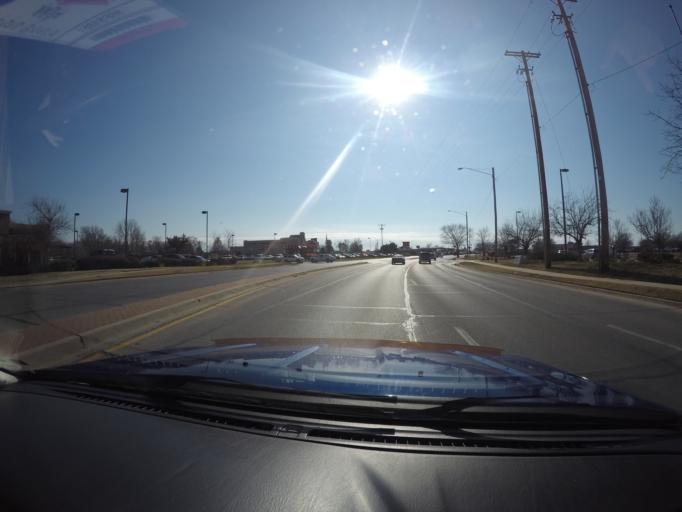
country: US
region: Kansas
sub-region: Sedgwick County
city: Wichita
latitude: 37.6787
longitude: -97.4260
